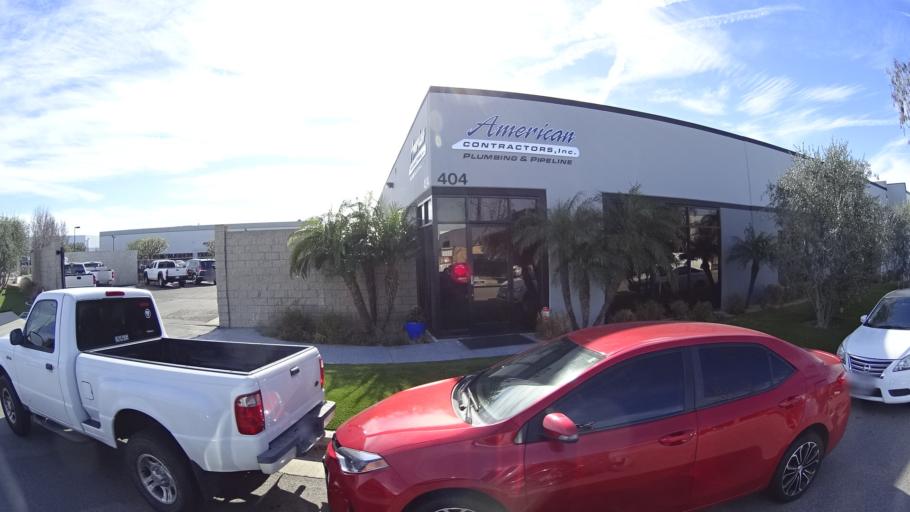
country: US
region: California
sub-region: Orange County
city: Orange
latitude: 33.8188
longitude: -117.8559
